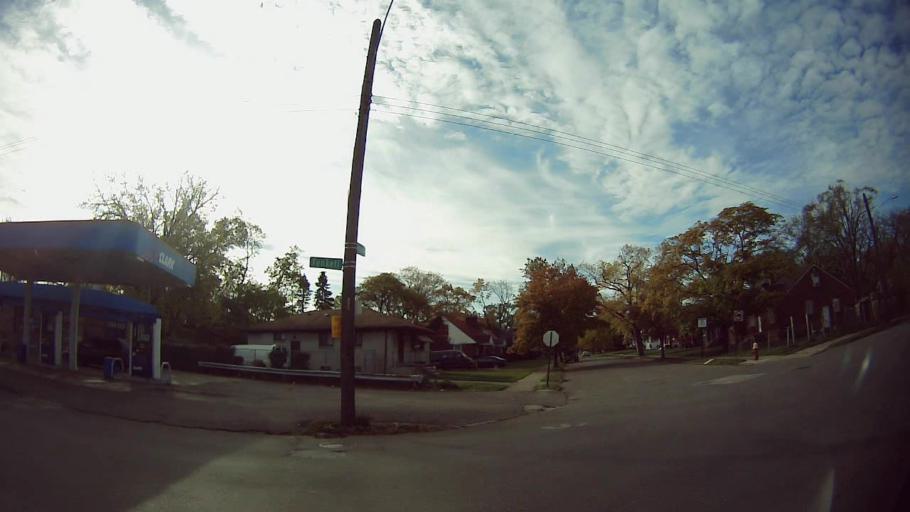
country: US
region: Michigan
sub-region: Oakland County
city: Oak Park
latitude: 42.4013
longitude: -83.2090
